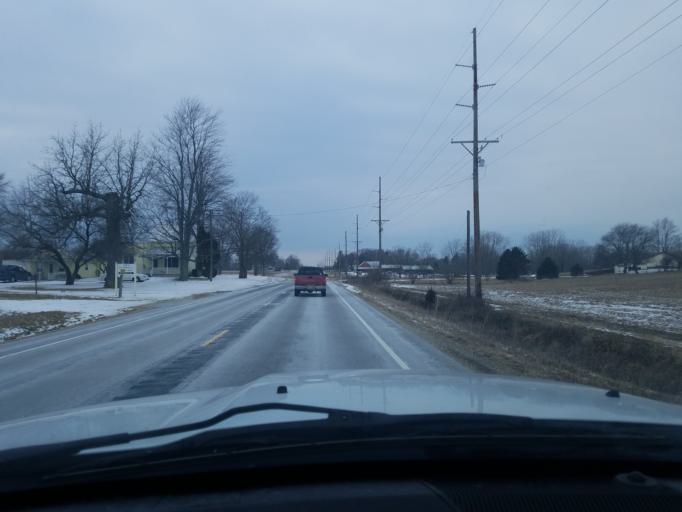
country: US
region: Indiana
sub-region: Randolph County
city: Farmland
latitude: 40.1714
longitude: -85.0586
